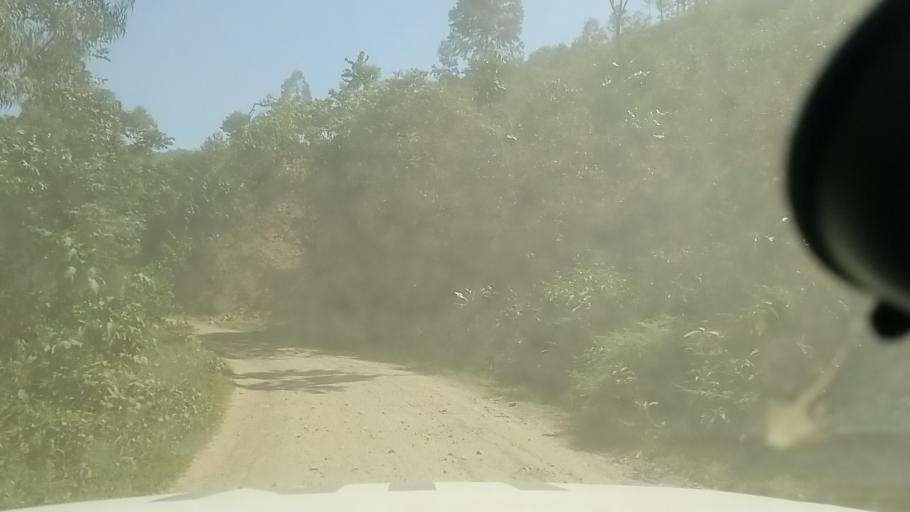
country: CD
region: Nord Kivu
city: Sake
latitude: -1.9515
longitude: 28.9276
